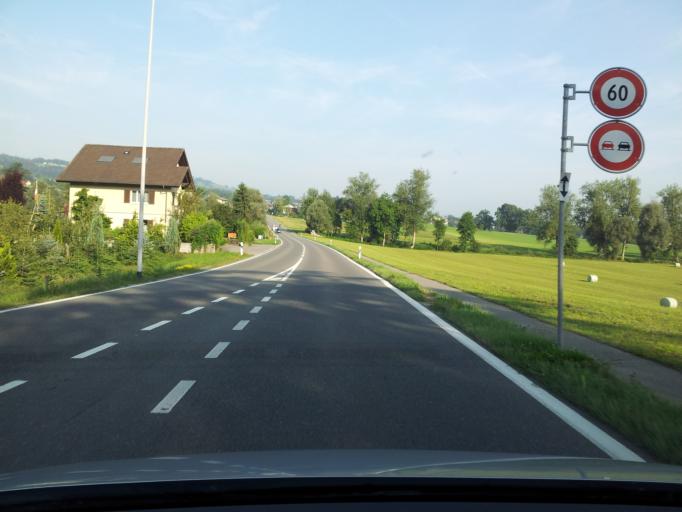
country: CH
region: Lucerne
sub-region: Sursee District
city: Neuenkirch
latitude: 47.0928
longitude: 8.2209
